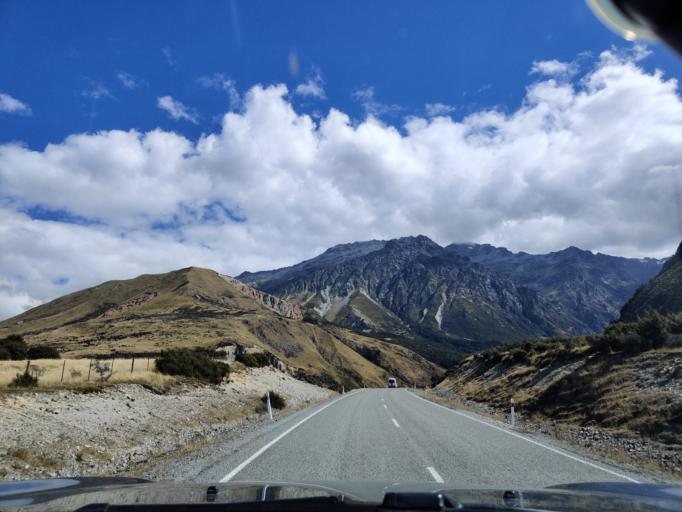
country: NZ
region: Canterbury
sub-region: Timaru District
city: Pleasant Point
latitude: -43.8583
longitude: 170.1082
